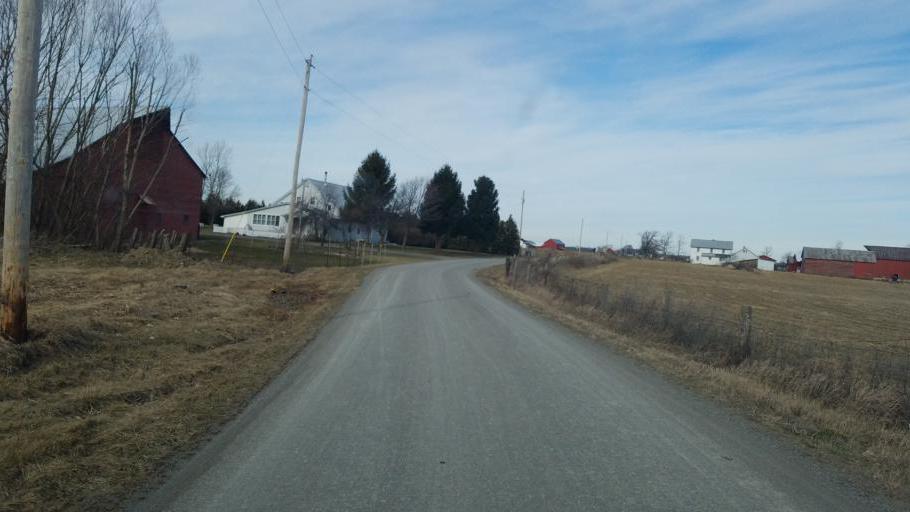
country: US
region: Ohio
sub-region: Hardin County
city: Kenton
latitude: 40.6034
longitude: -83.5554
